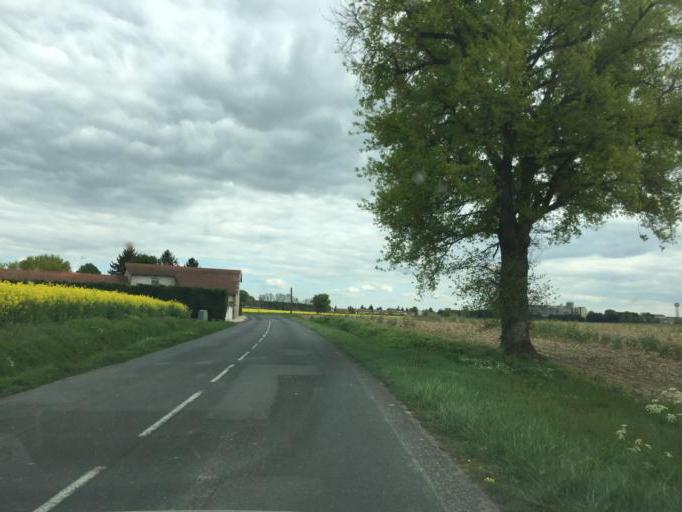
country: FR
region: Rhone-Alpes
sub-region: Departement de l'Ain
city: Saint-Andre-de-Corcy
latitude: 45.9367
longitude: 4.9450
